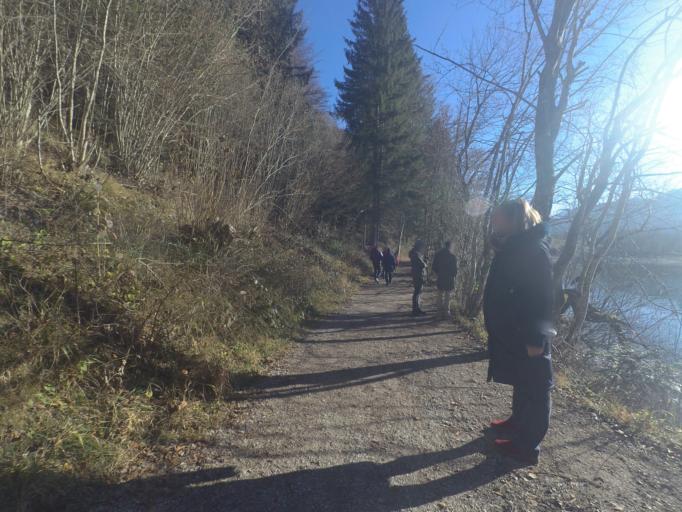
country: AT
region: Salzburg
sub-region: Politischer Bezirk Salzburg-Umgebung
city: Faistenau
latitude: 47.7521
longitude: 13.2510
